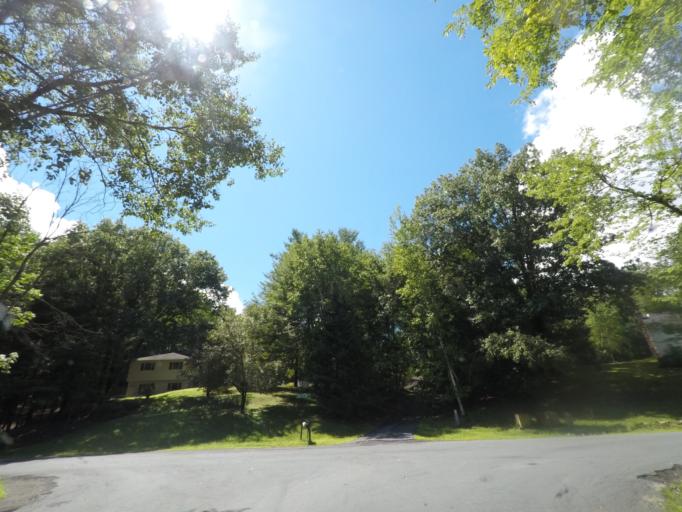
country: US
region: New York
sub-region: Rensselaer County
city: Averill Park
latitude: 42.6292
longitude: -73.5777
